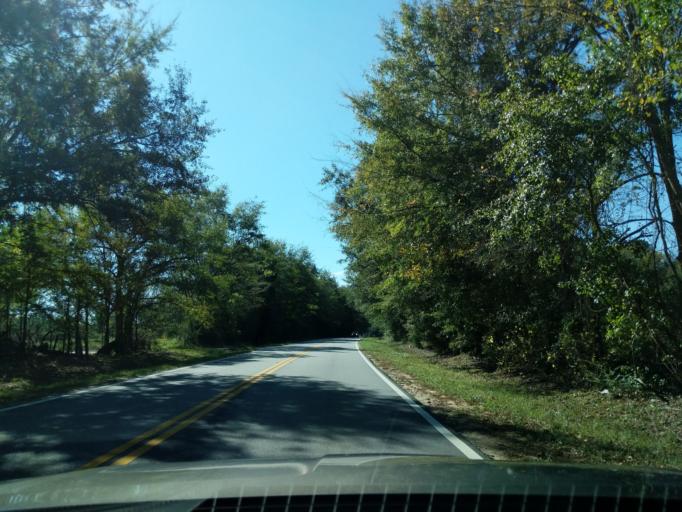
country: US
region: Georgia
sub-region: Richmond County
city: Hephzibah
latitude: 33.3073
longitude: -82.0181
